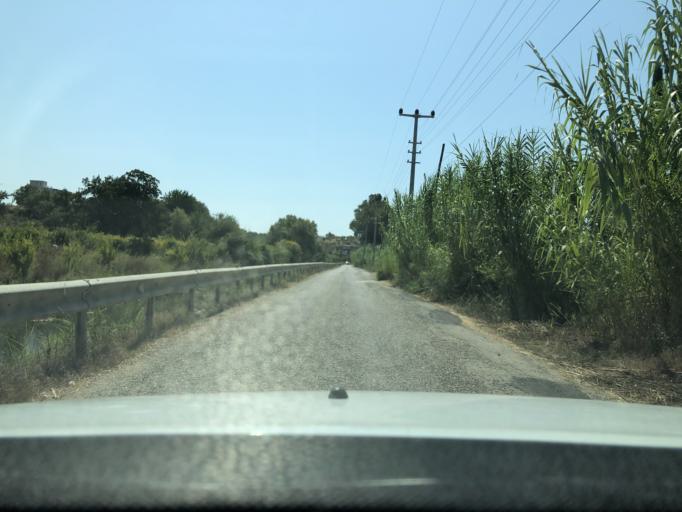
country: TR
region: Antalya
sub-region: Manavgat
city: Manavgat
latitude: 36.8051
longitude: 31.4667
